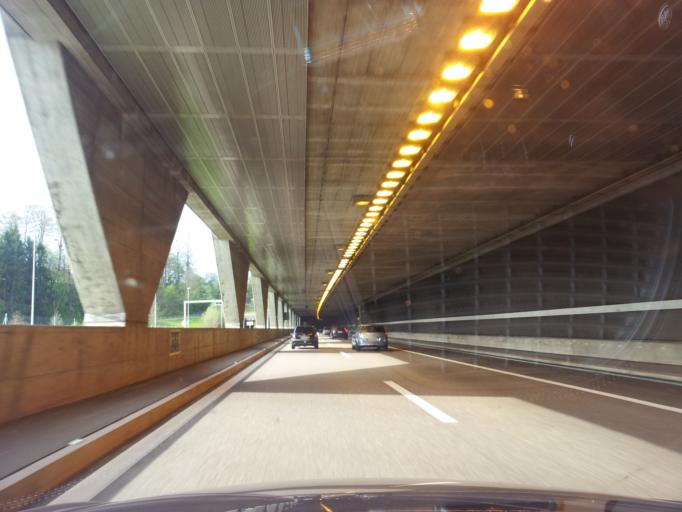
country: CH
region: Solothurn
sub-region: Bezirk Wasseramt
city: Zuchwil
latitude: 47.2007
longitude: 7.5658
